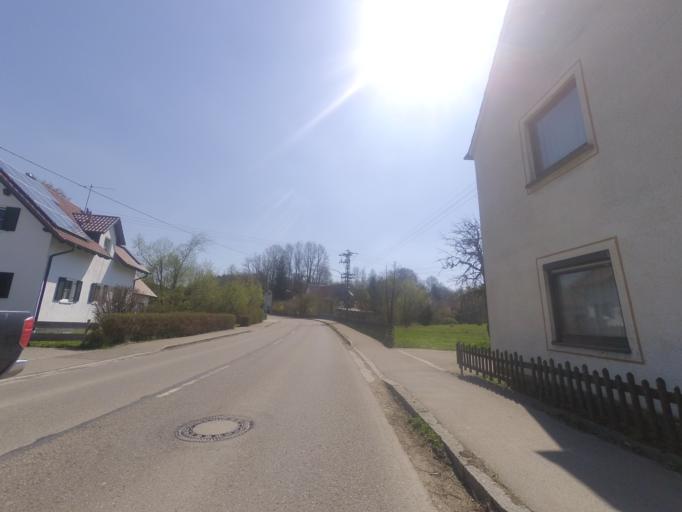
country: DE
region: Bavaria
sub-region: Swabia
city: Roggenburg
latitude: 48.2881
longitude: 10.2162
